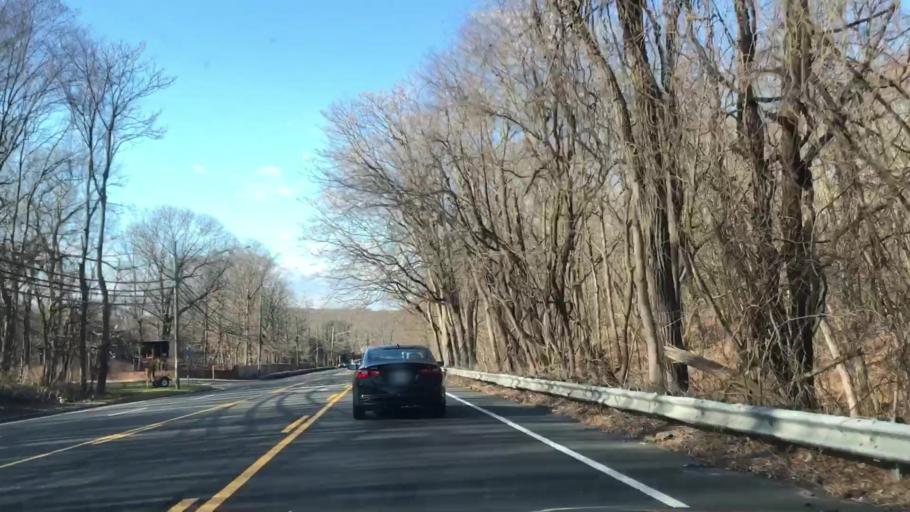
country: US
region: New York
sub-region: Suffolk County
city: Elwood
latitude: 40.8297
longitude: -73.3562
